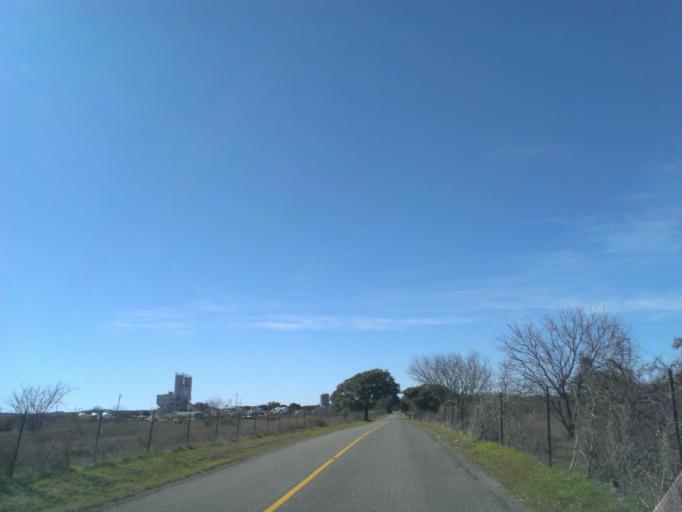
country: US
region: Texas
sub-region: Burnet County
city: Marble Falls
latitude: 30.4747
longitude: -98.1786
